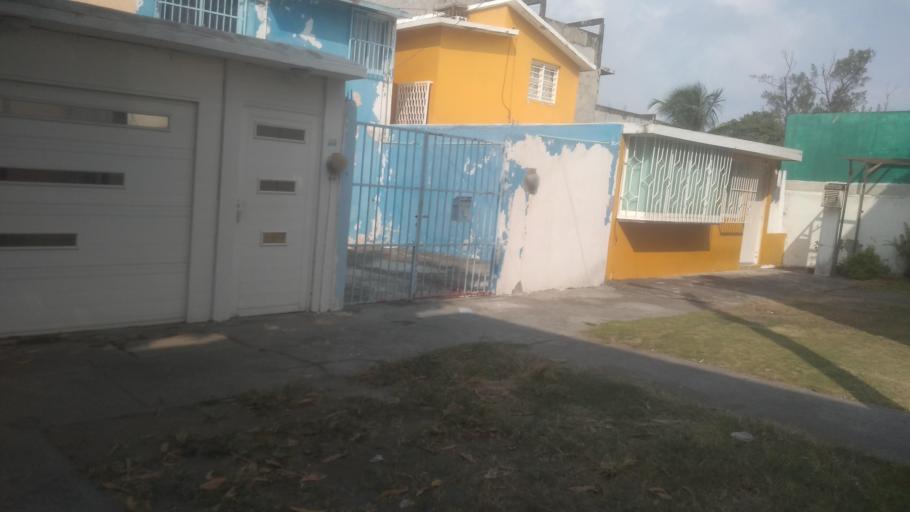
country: MX
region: Veracruz
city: Veracruz
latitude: 19.2058
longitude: -96.1680
